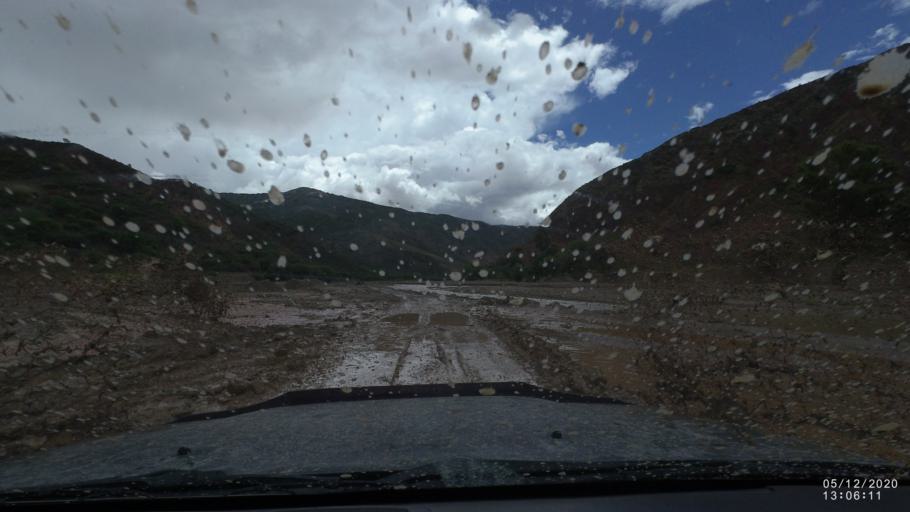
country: BO
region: Cochabamba
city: Sipe Sipe
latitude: -17.5571
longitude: -66.4439
